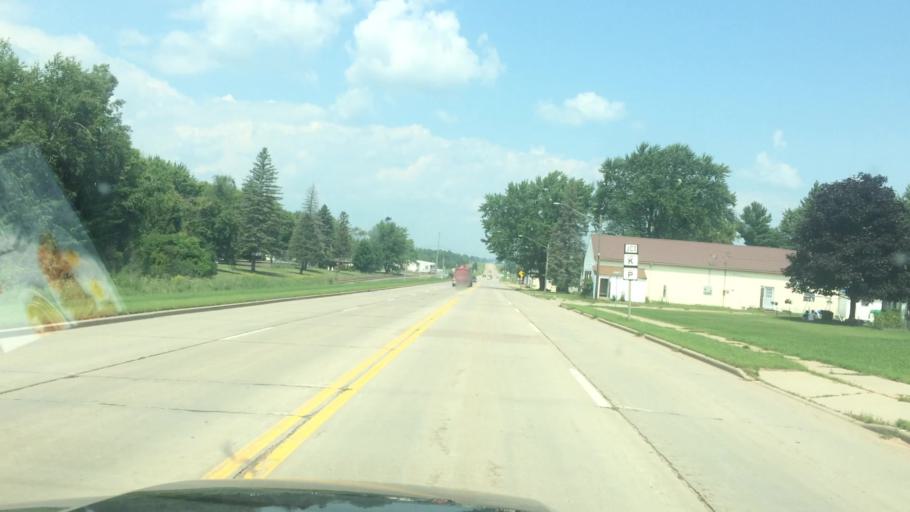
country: US
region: Wisconsin
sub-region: Clark County
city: Colby
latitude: 44.8489
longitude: -90.3160
